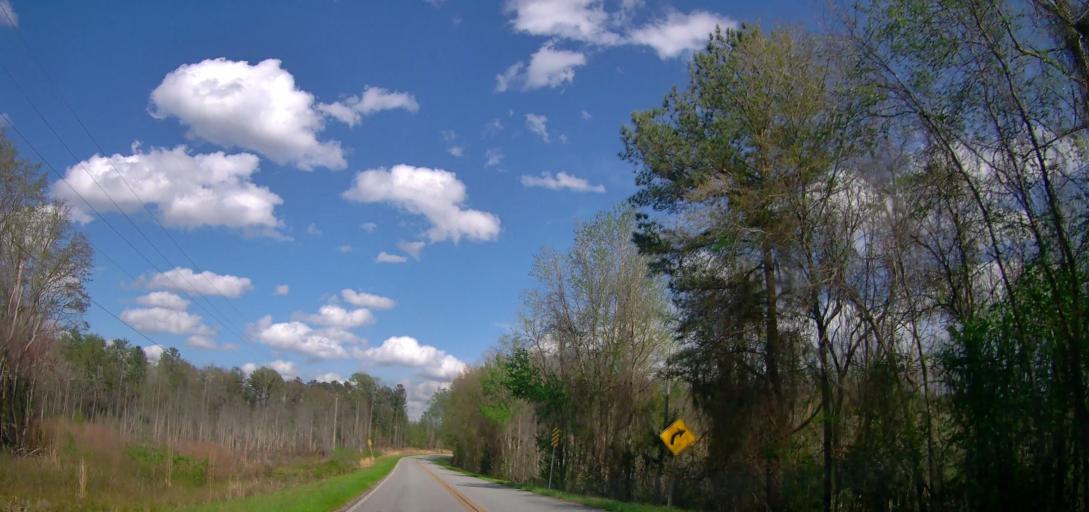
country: US
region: Georgia
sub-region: Wilkinson County
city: Gordon
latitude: 32.8259
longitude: -83.4208
